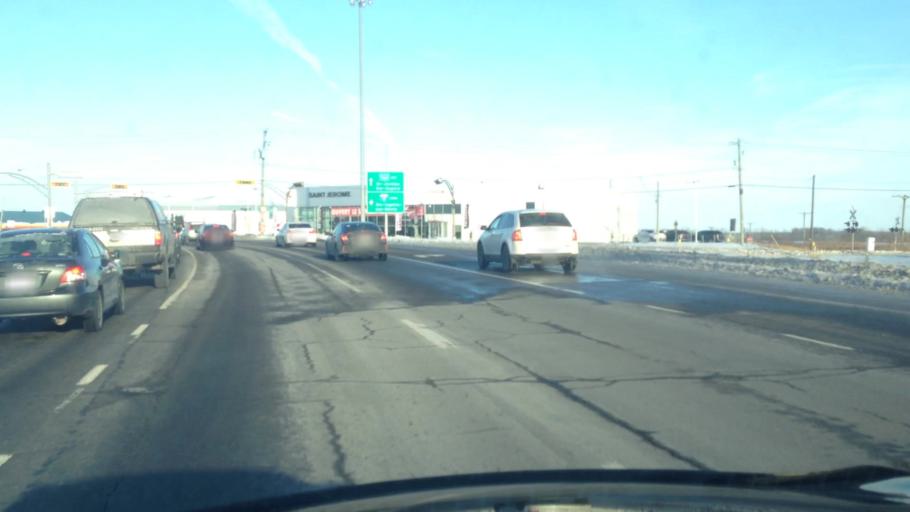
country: CA
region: Quebec
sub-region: Laurentides
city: Saint-Jerome
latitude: 45.7458
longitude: -74.0017
